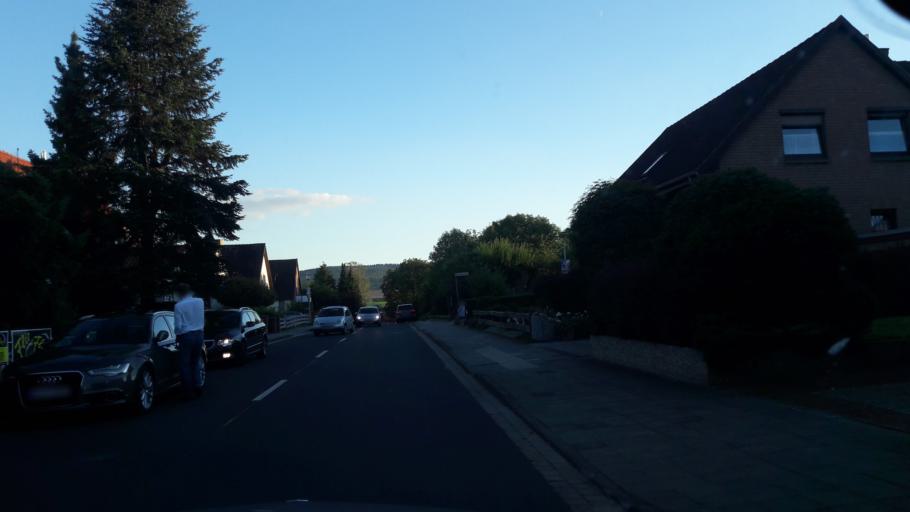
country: DE
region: Lower Saxony
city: Hildesheim
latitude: 52.1155
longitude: 9.9945
